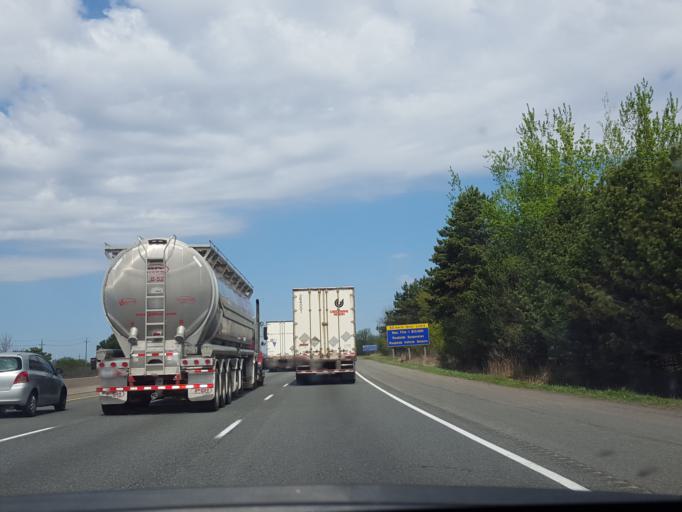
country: CA
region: Ontario
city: Oshawa
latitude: 43.8787
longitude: -78.8028
